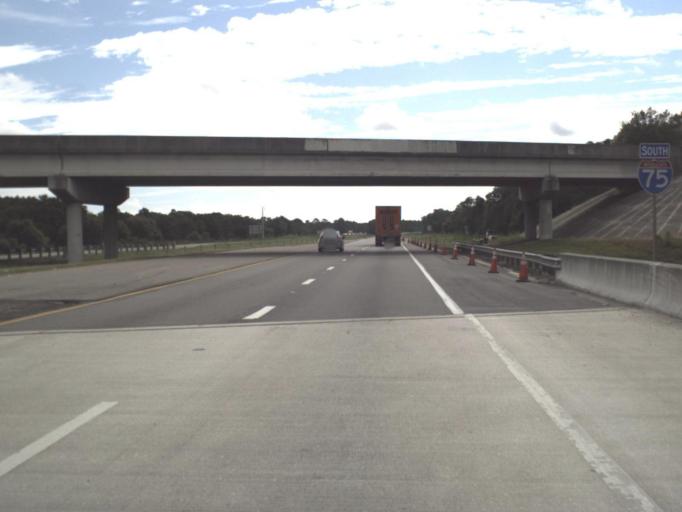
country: US
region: Florida
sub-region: Sarasota County
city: Plantation
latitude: 27.1110
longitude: -82.3391
